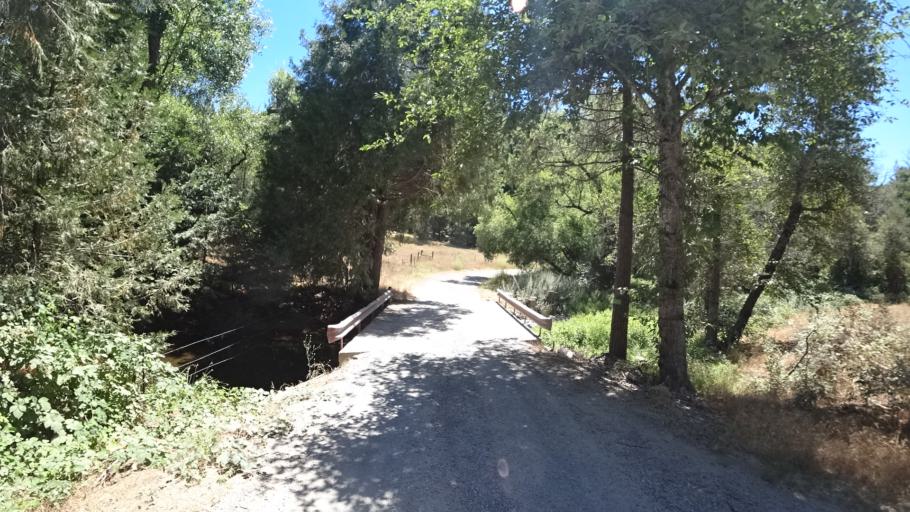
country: US
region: California
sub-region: Calaveras County
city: Mountain Ranch
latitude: 38.2772
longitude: -120.4532
